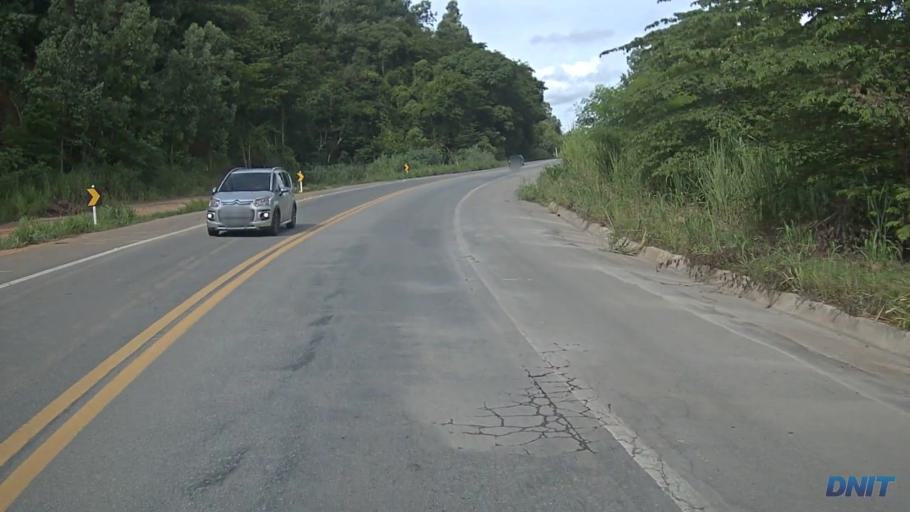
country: BR
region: Minas Gerais
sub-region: Ipaba
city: Ipaba
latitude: -19.3246
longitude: -42.4180
